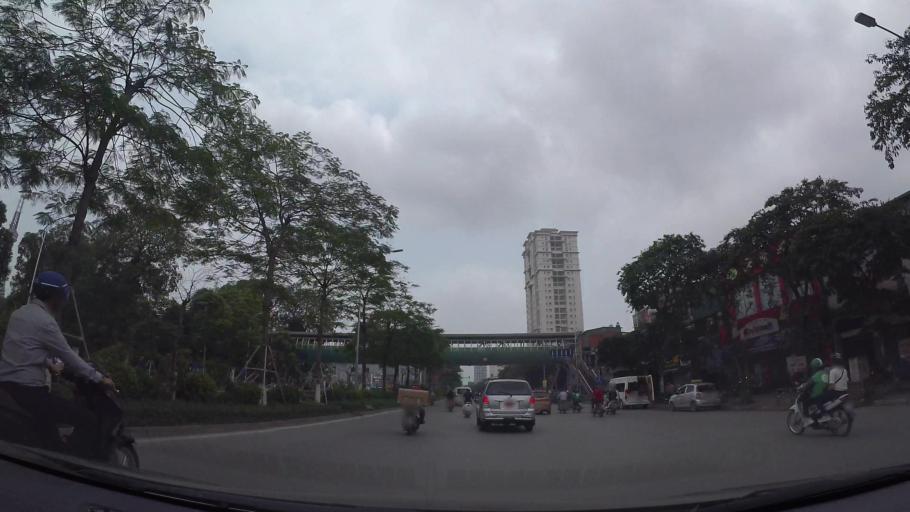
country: VN
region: Ha Noi
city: Hai BaTrung
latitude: 21.0078
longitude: 105.8449
